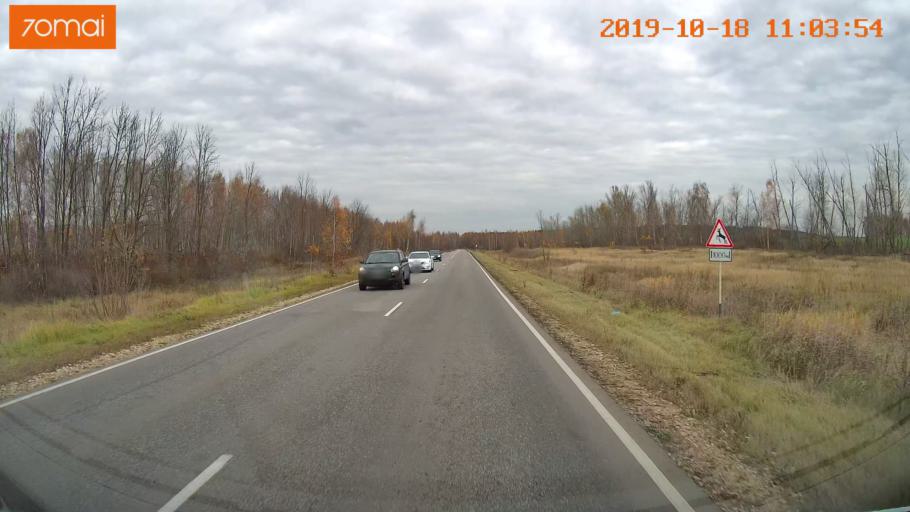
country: RU
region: Tula
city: Yepifan'
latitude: 53.8867
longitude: 38.5498
